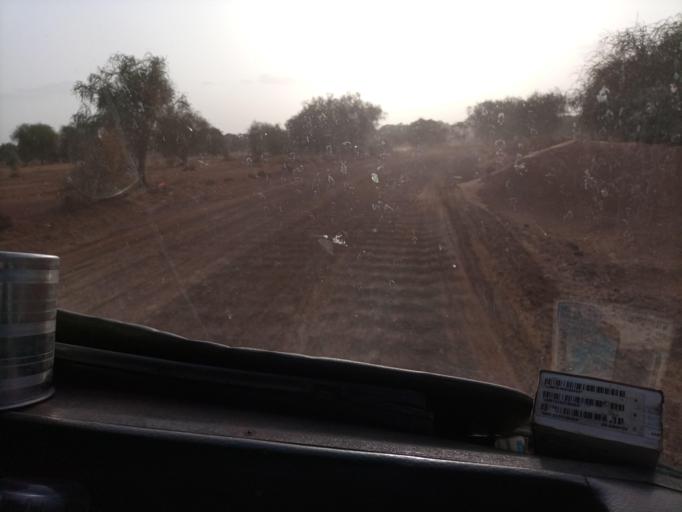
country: SN
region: Louga
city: Dara
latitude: 15.3549
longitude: -15.5326
